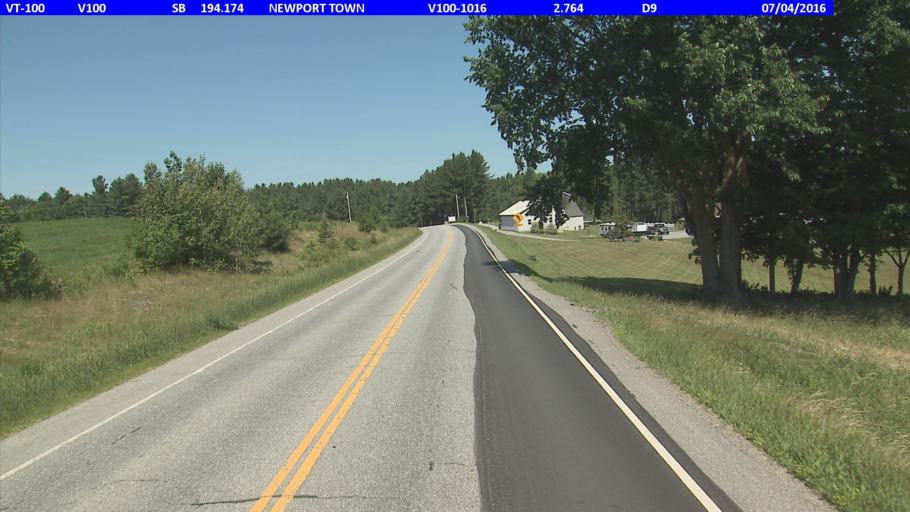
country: US
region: Vermont
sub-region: Orleans County
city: Newport
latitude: 44.9208
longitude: -72.2983
